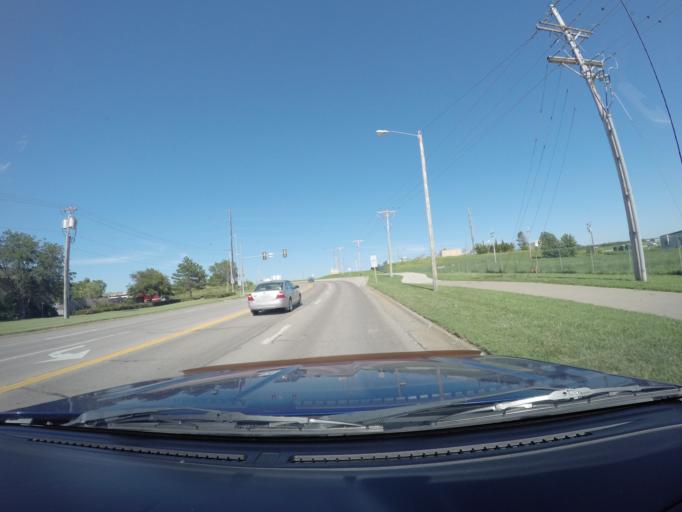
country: US
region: Kansas
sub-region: Riley County
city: Manhattan
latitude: 39.2042
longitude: -96.5850
